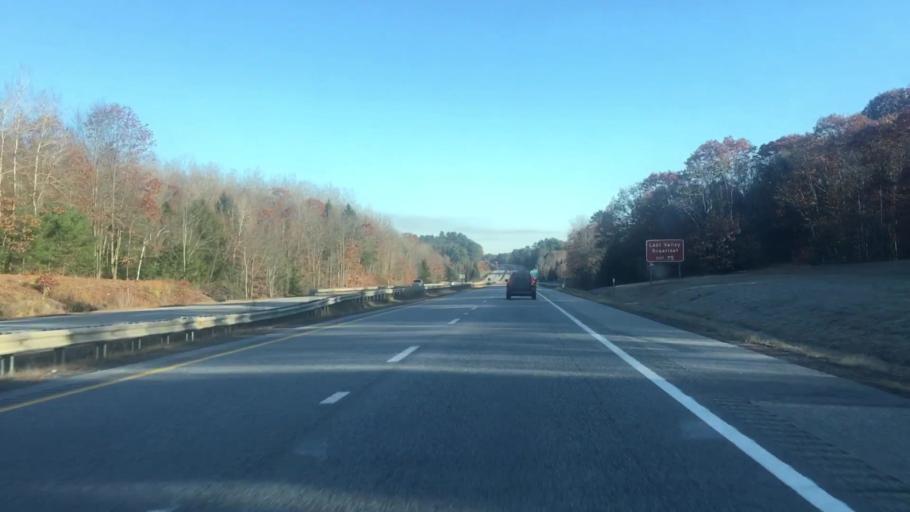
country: US
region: Maine
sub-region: Cumberland County
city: New Gloucester
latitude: 44.0091
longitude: -70.3026
